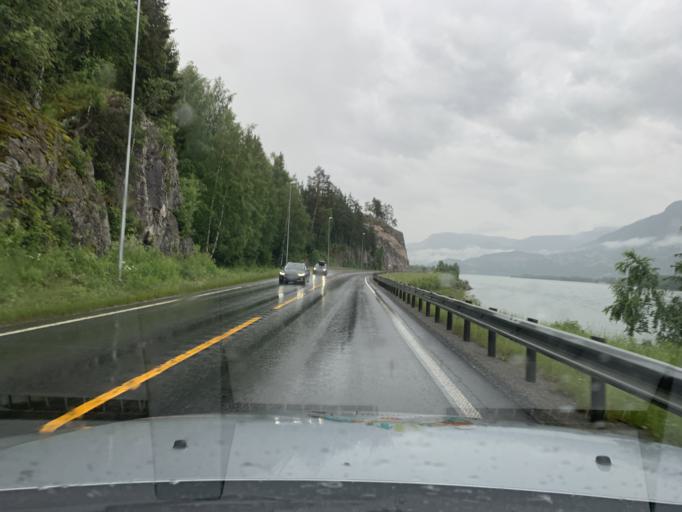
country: NO
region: Oppland
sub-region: Ringebu
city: Ringebu
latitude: 61.4853
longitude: 10.1814
